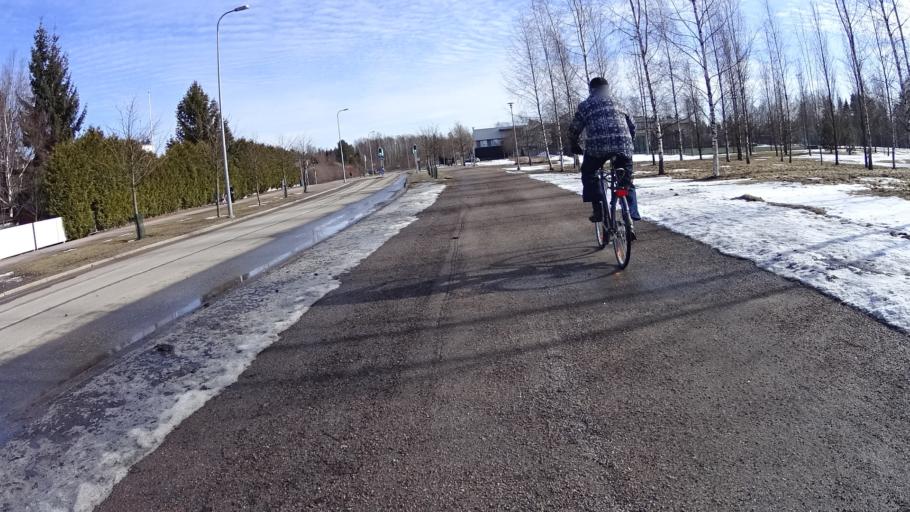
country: FI
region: Uusimaa
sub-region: Helsinki
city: Kilo
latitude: 60.2342
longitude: 24.8170
